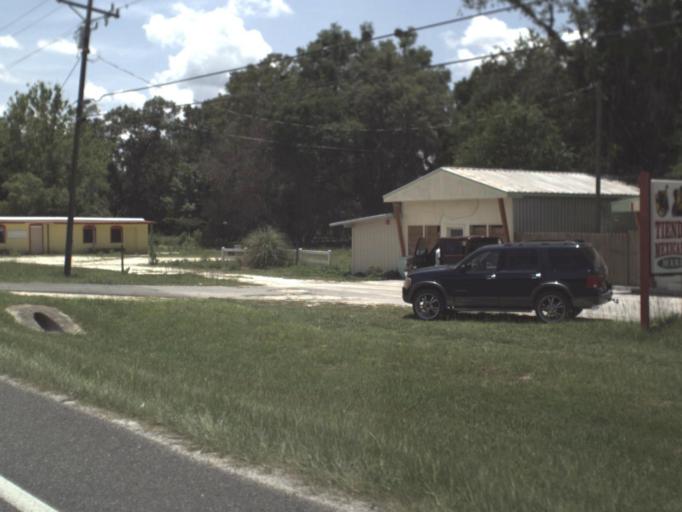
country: US
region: Florida
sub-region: Levy County
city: Manatee Road
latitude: 29.5820
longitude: -82.9196
